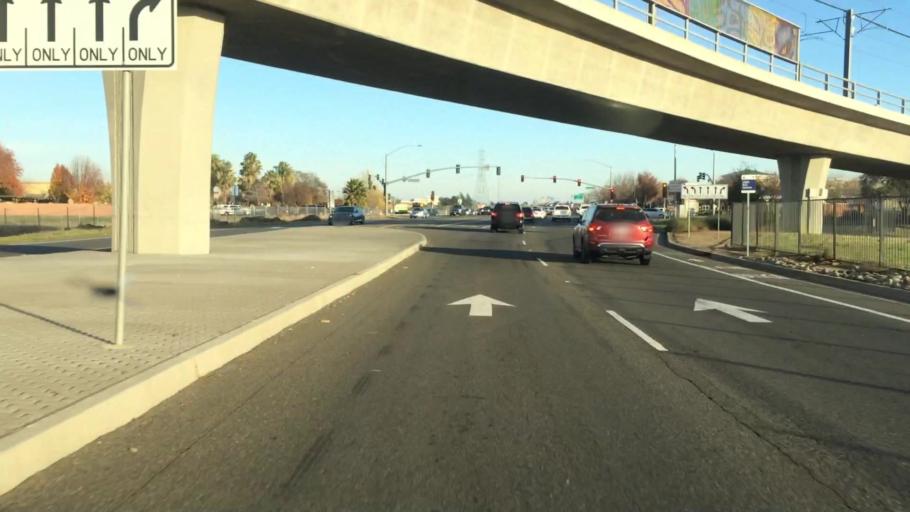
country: US
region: California
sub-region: Sacramento County
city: Laguna
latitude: 38.4579
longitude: -121.4193
